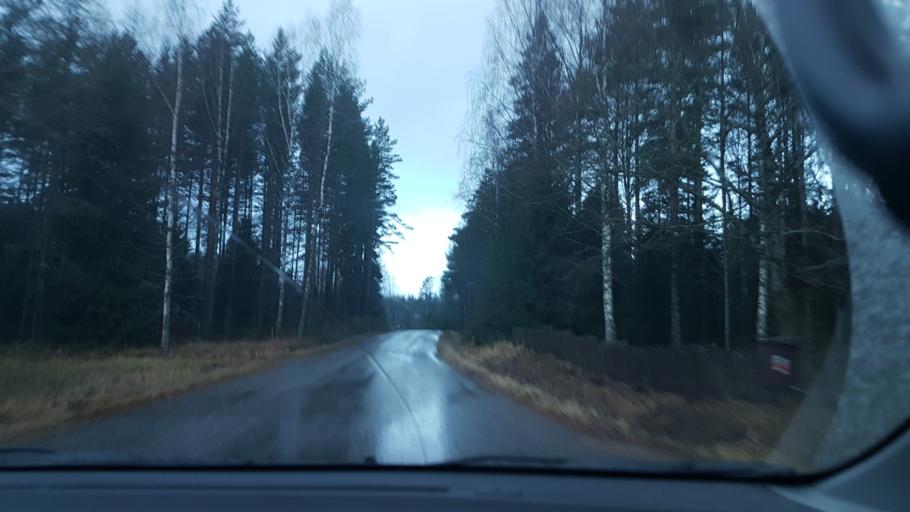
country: FI
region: Uusimaa
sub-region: Helsinki
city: Lohja
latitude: 60.2154
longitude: 24.0932
